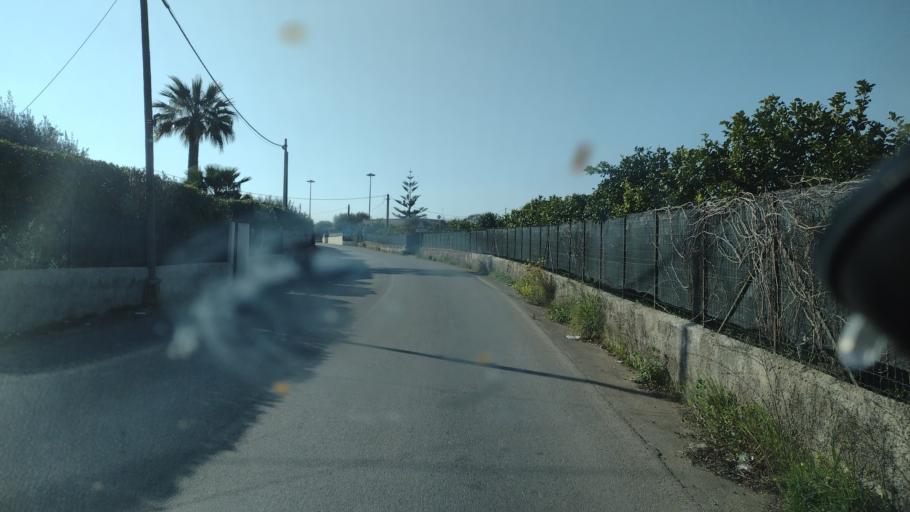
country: IT
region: Sicily
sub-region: Provincia di Siracusa
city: Avola
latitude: 36.8731
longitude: 15.1268
